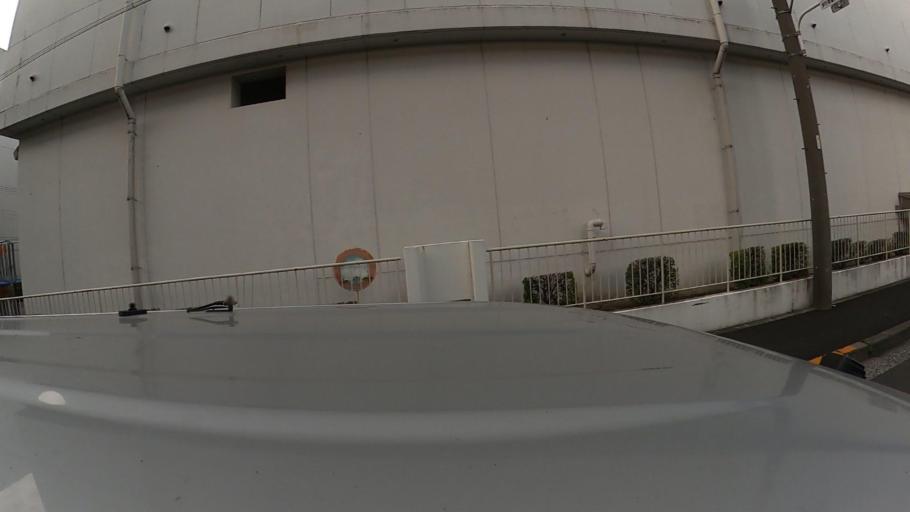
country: JP
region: Kanagawa
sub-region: Kawasaki-shi
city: Kawasaki
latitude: 35.5781
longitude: 139.7506
